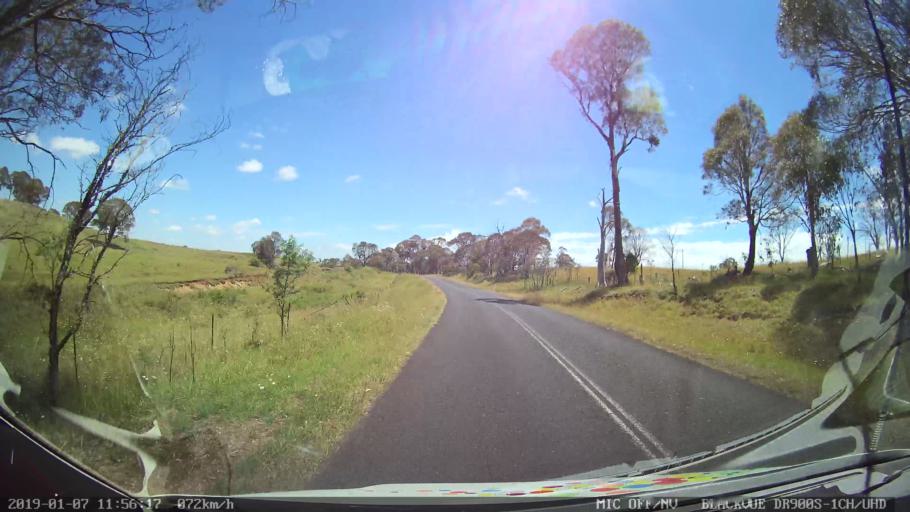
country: AU
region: New South Wales
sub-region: Guyra
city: Guyra
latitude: -30.2763
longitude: 151.6740
